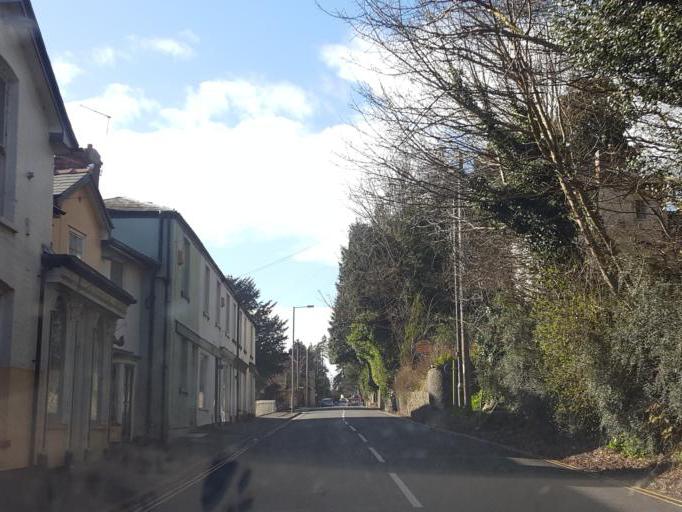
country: GB
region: England
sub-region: Worcestershire
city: Great Malvern
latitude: 52.0794
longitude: -2.3324
